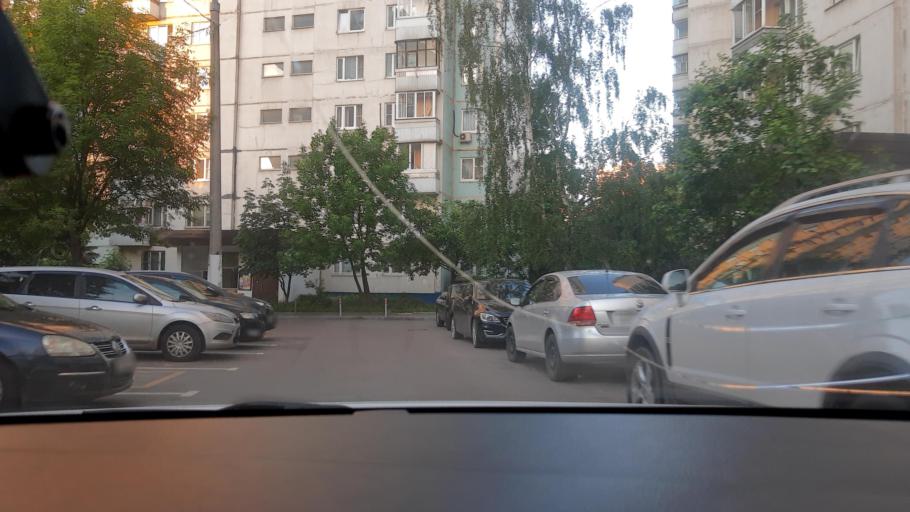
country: RU
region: Moscow
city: Solntsevo
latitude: 55.6477
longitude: 37.4058
